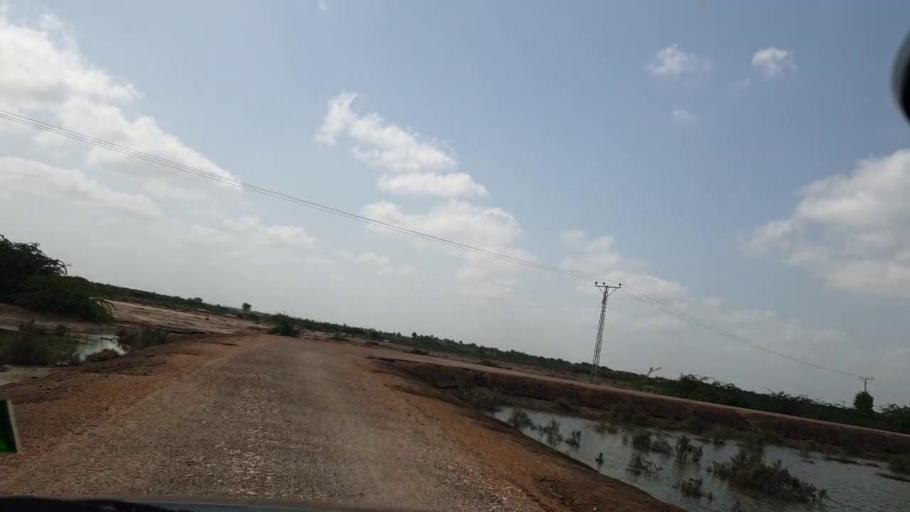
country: PK
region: Sindh
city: Kadhan
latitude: 24.5847
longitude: 69.1554
